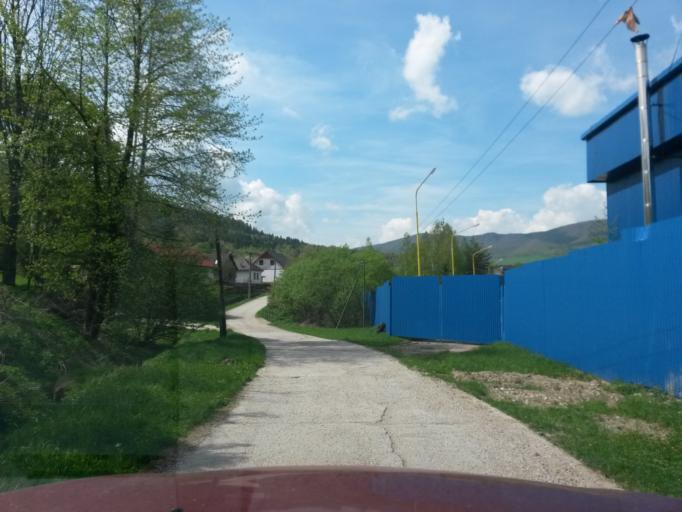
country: SK
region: Kosicky
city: Gelnica
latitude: 48.8148
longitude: 20.8920
